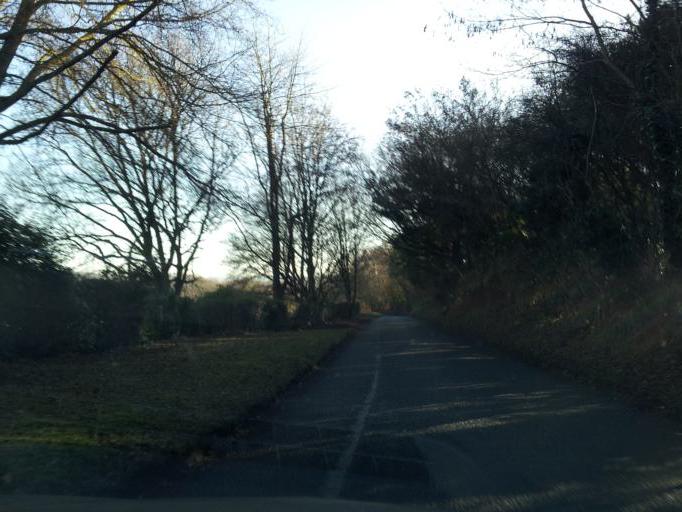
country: GB
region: England
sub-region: Suffolk
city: Sudbury
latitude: 51.9747
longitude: 0.7620
